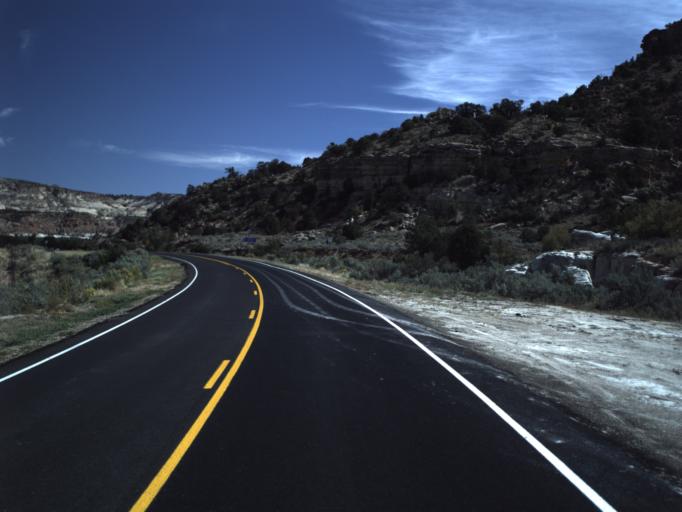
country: US
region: Utah
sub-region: Wayne County
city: Loa
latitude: 37.7758
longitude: -111.6331
